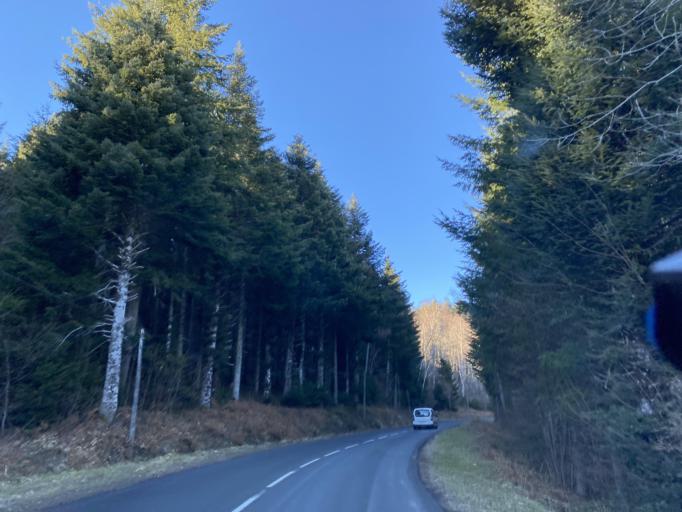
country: FR
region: Auvergne
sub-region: Departement du Puy-de-Dome
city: Celles-sur-Durolle
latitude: 45.7629
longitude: 3.6453
